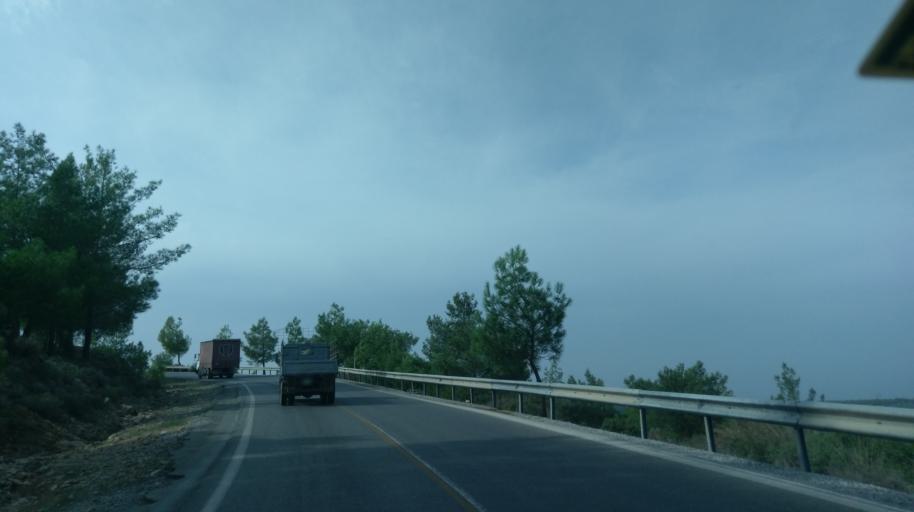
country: CY
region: Lefkosia
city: Morfou
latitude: 35.2537
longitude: 33.0337
